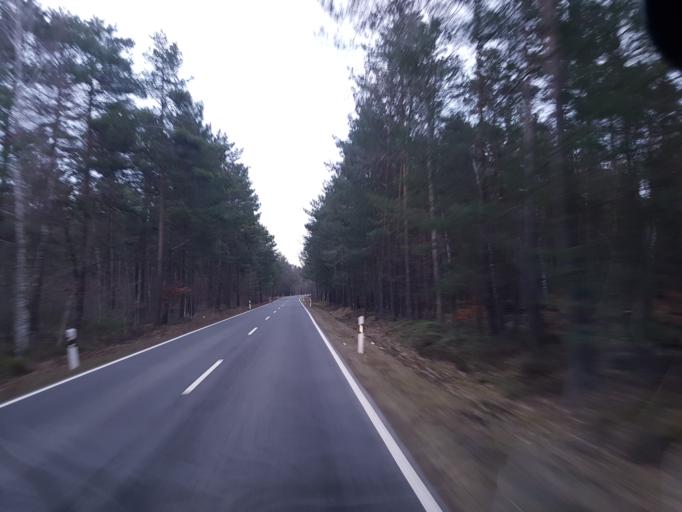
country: DE
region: Brandenburg
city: Sallgast
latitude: 51.5784
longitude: 13.8275
